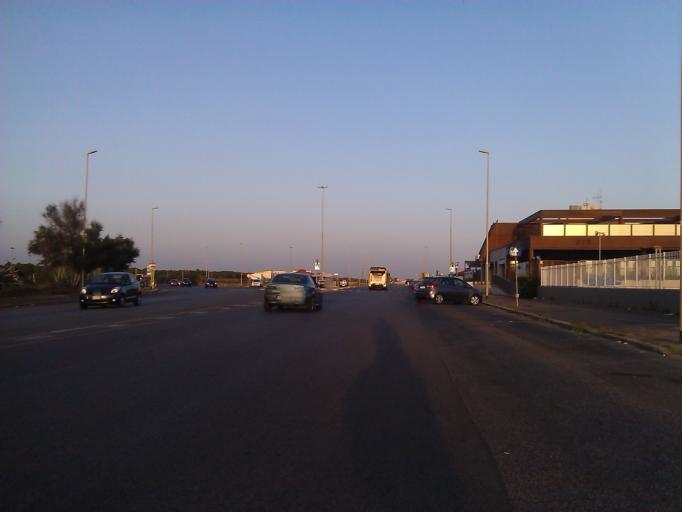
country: IT
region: Latium
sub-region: Citta metropolitana di Roma Capitale
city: Lido di Ostia
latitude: 41.7136
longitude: 12.3188
